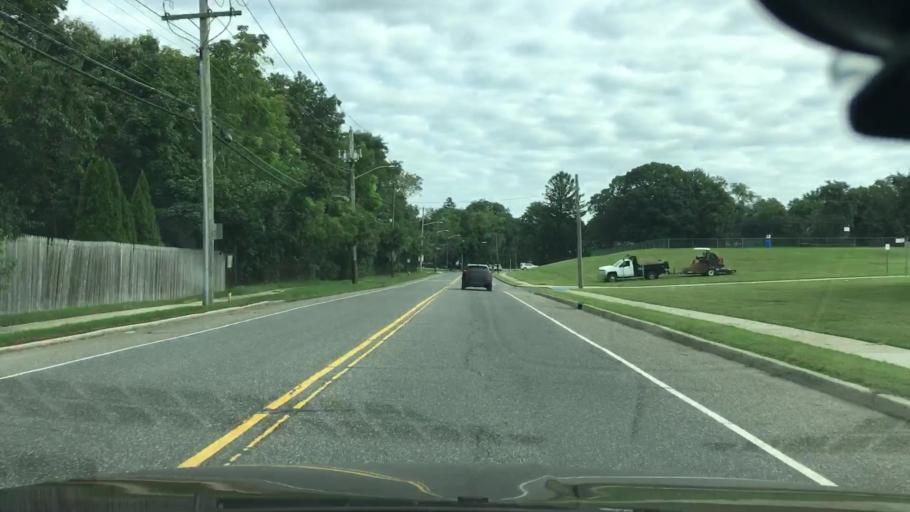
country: US
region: New York
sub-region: Nassau County
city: Old Bethpage
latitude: 40.7690
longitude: -73.4516
